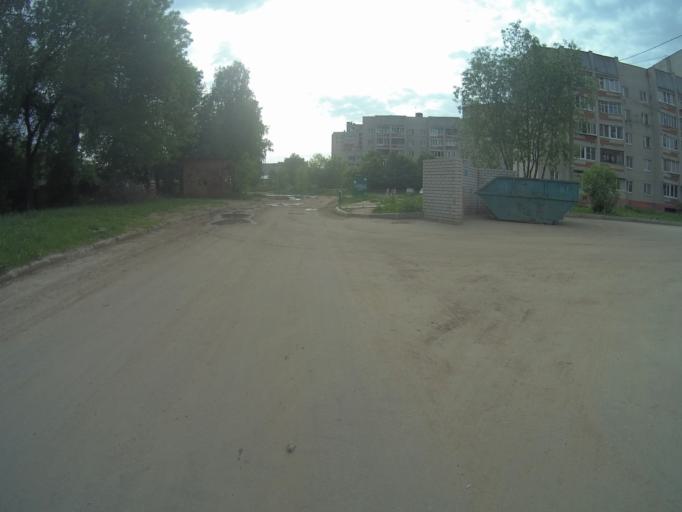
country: RU
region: Vladimir
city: Kommunar
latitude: 56.1653
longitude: 40.4629
